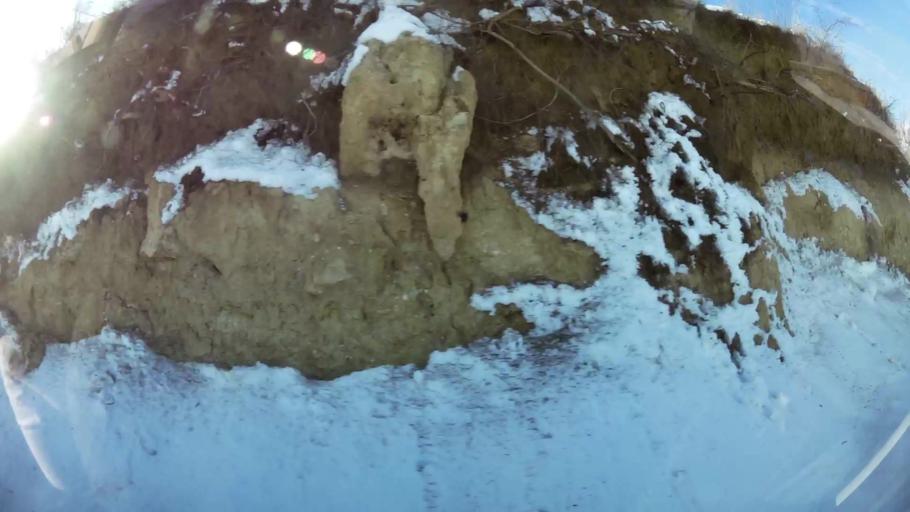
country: MK
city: Ljubin
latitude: 41.9808
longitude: 21.3017
